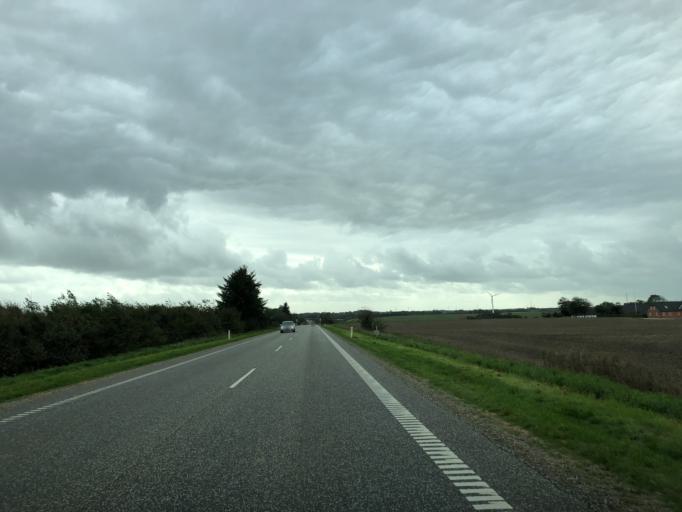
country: DK
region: North Denmark
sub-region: Thisted Kommune
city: Thisted
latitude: 56.9079
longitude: 8.6055
